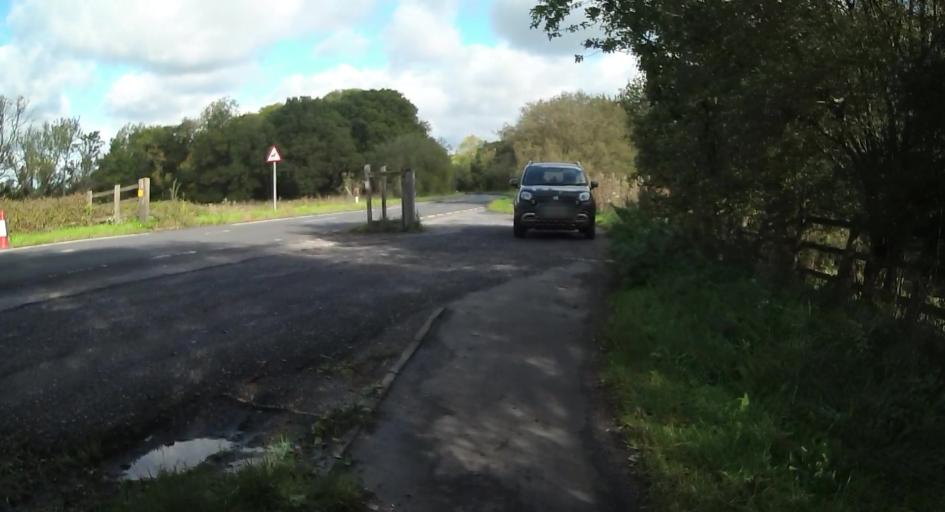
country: GB
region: England
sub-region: Hampshire
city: Odiham
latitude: 51.2615
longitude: -0.9295
